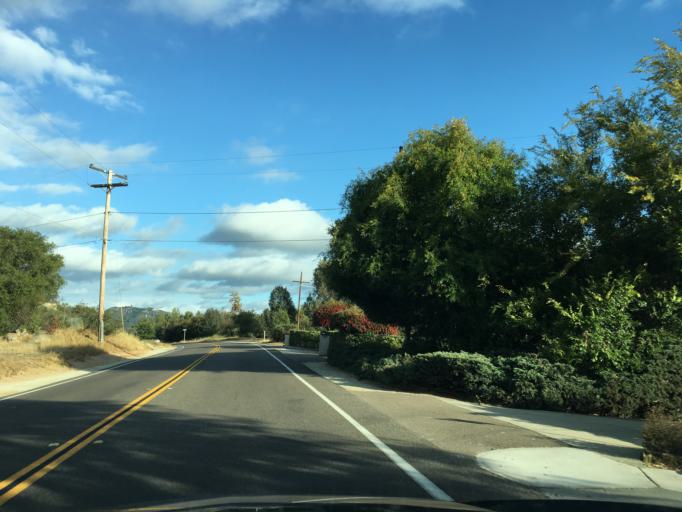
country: US
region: California
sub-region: San Diego County
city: Valley Center
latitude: 33.2314
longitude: -117.0457
